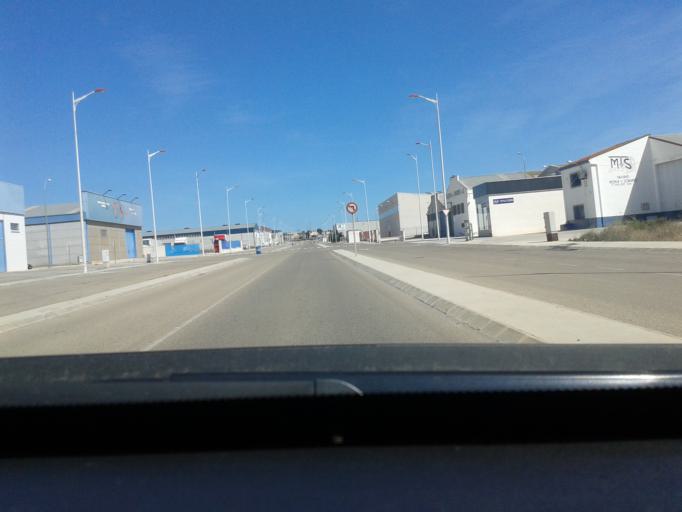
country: ES
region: Castille-La Mancha
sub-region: Provincia de Albacete
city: Caudete
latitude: 38.7114
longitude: -0.9730
